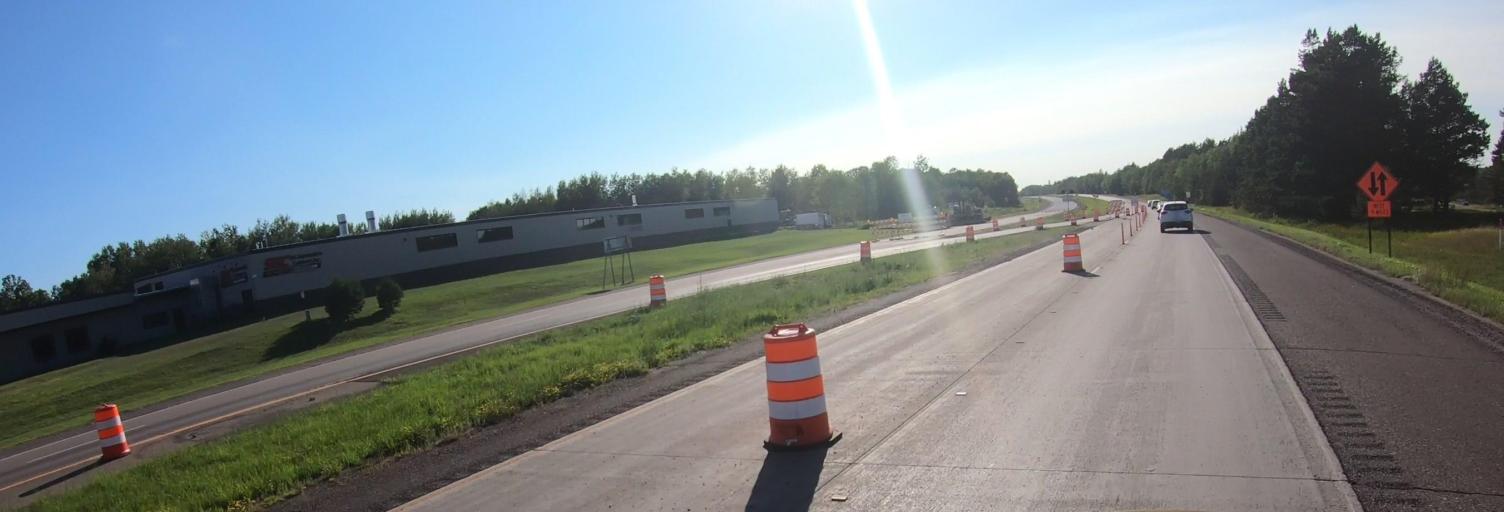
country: US
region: Minnesota
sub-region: Saint Louis County
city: Hermantown
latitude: 46.8513
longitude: -92.2868
